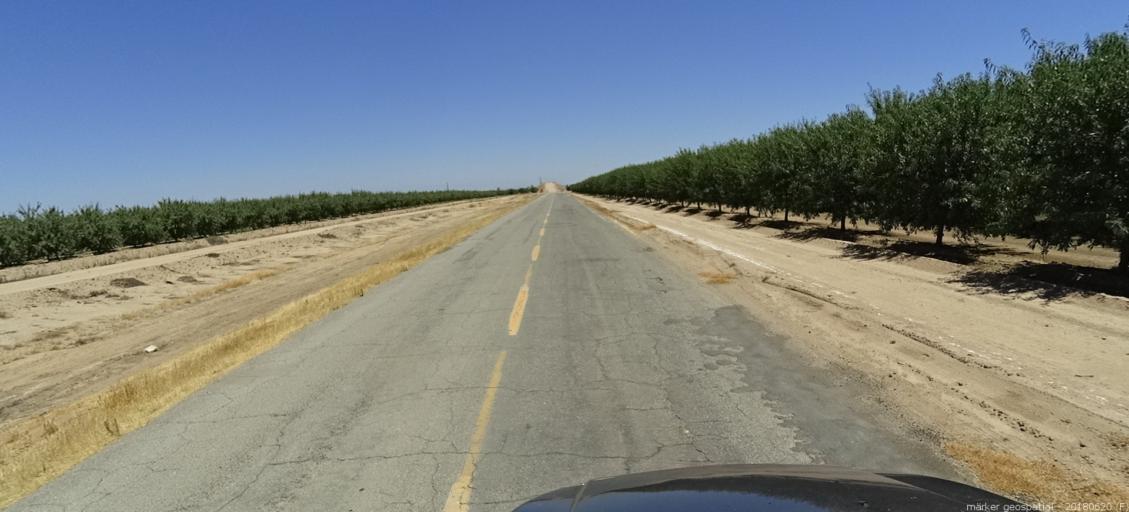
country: US
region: California
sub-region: Madera County
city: Parksdale
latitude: 36.9093
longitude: -119.9868
